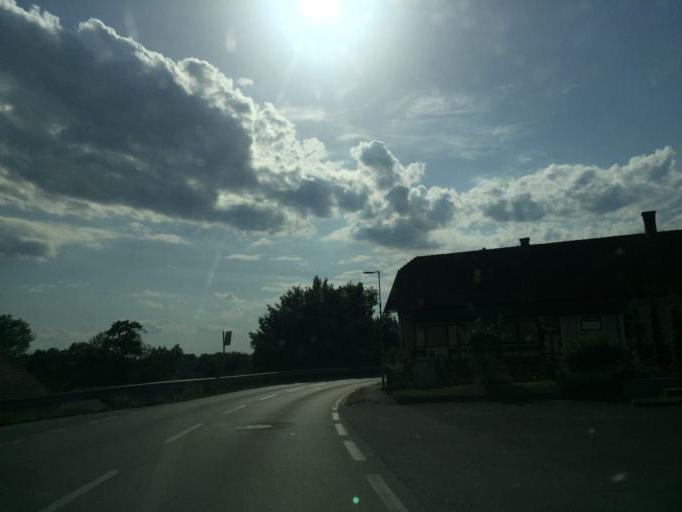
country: AT
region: Styria
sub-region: Politischer Bezirk Suedoststeiermark
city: Halbenrain
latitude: 46.7219
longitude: 15.9459
